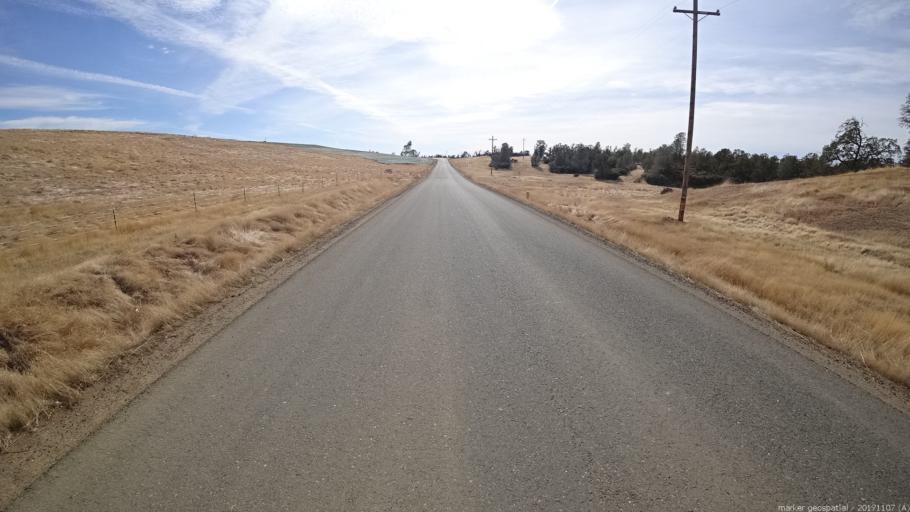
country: US
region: California
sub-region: Shasta County
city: Shasta
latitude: 40.4829
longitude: -122.5385
